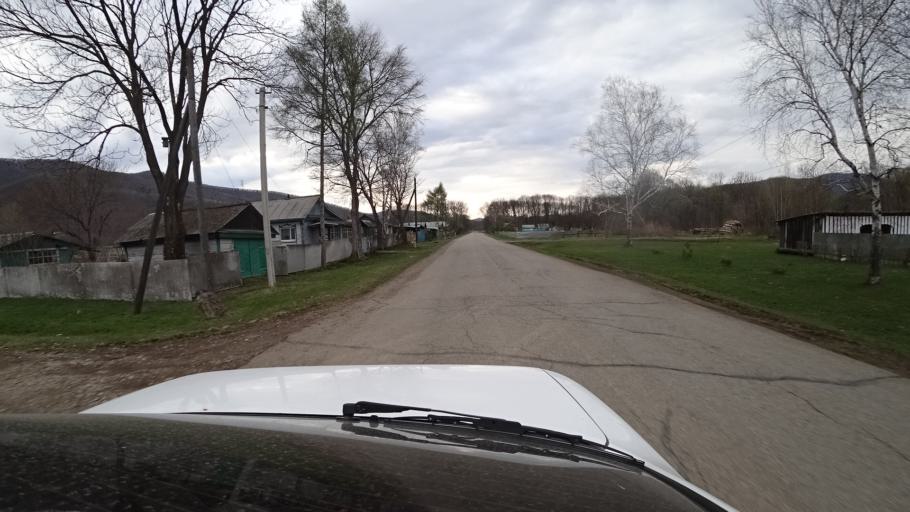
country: RU
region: Primorskiy
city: Novopokrovka
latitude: 45.1454
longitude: 134.3842
